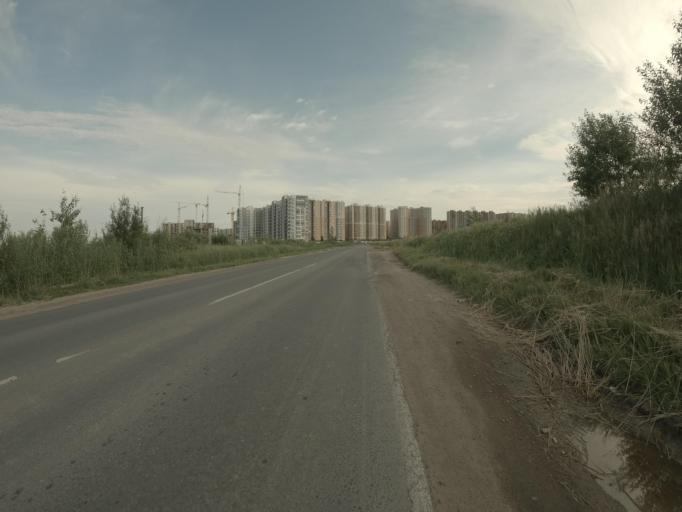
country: RU
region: St.-Petersburg
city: Krasnogvargeisky
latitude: 59.9240
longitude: 30.5177
